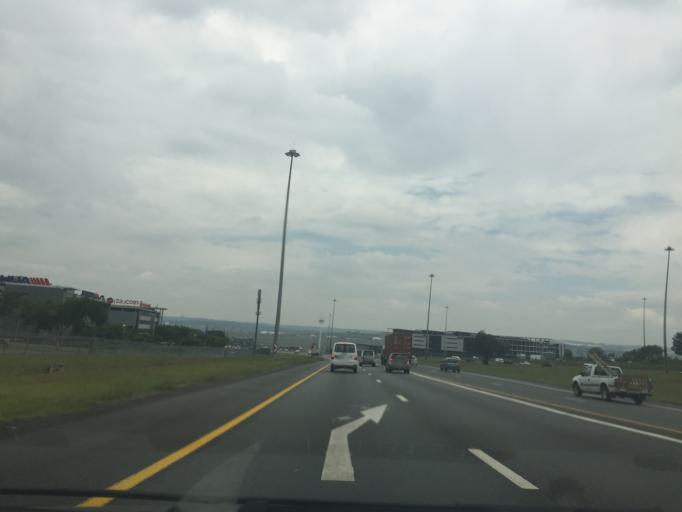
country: ZA
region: Gauteng
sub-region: City of Johannesburg Metropolitan Municipality
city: Midrand
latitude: -26.0450
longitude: 28.0960
